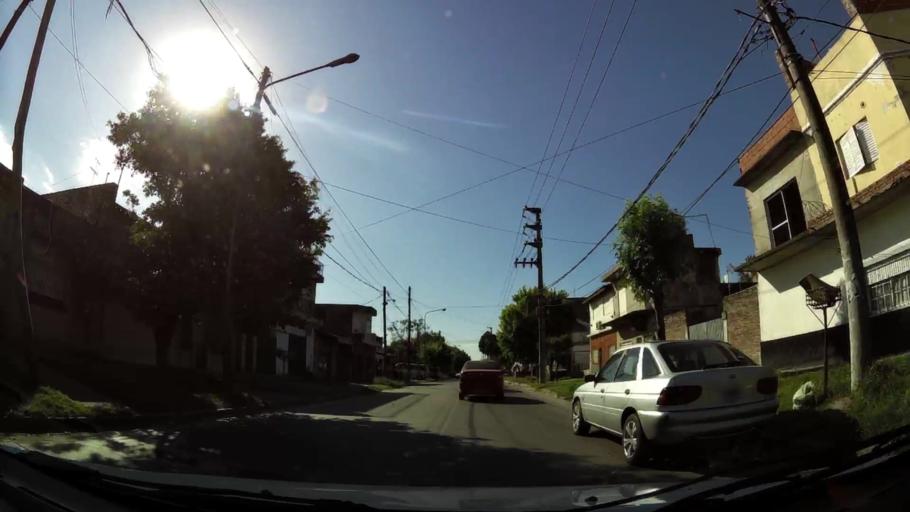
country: AR
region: Buenos Aires
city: Hurlingham
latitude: -34.5606
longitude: -58.6164
